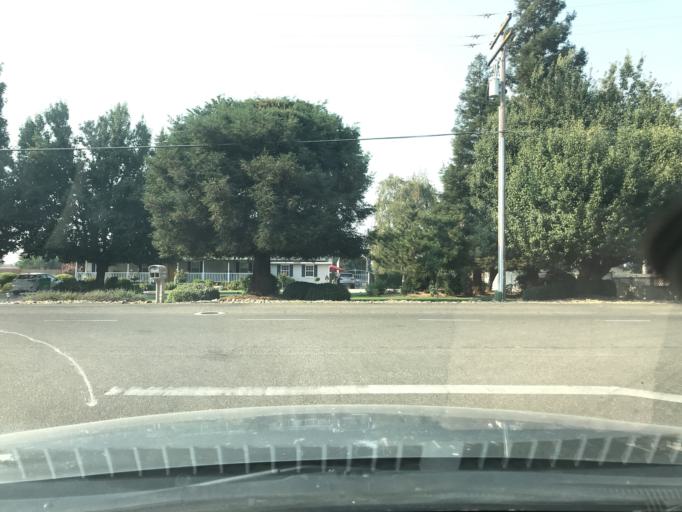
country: US
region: California
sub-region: Merced County
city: Atwater
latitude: 37.3238
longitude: -120.5986
